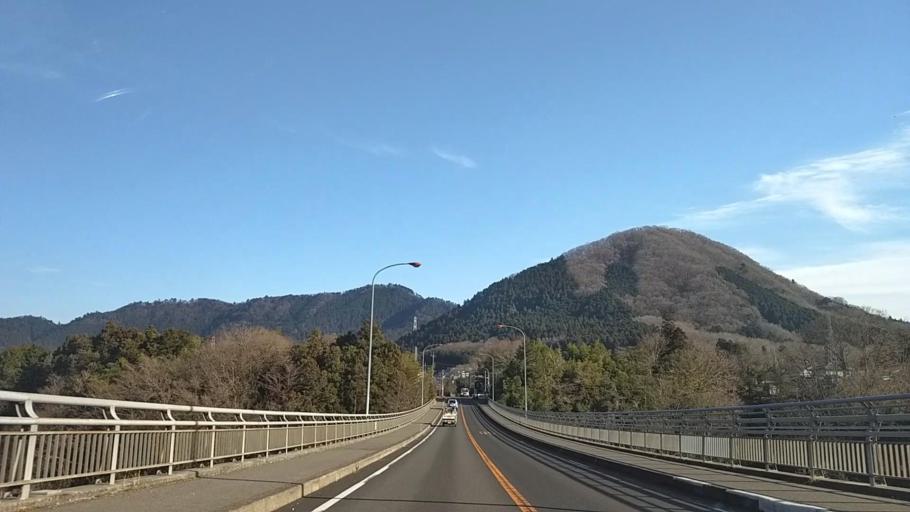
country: JP
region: Yamanashi
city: Uenohara
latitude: 35.5643
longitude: 139.2028
